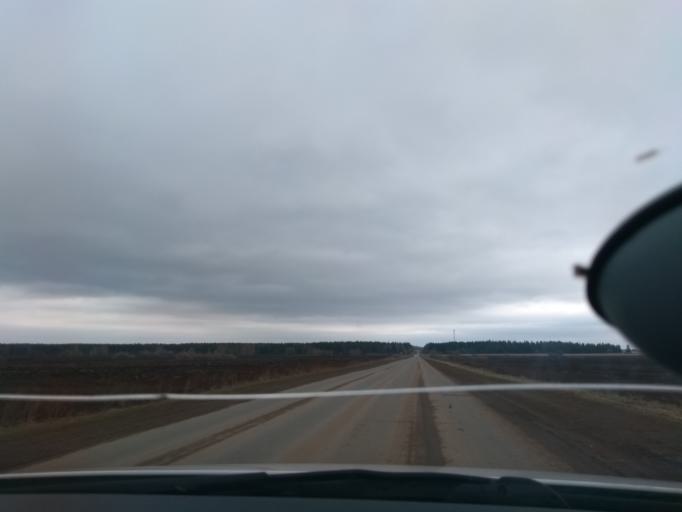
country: RU
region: Perm
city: Kungur
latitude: 57.3879
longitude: 56.8625
